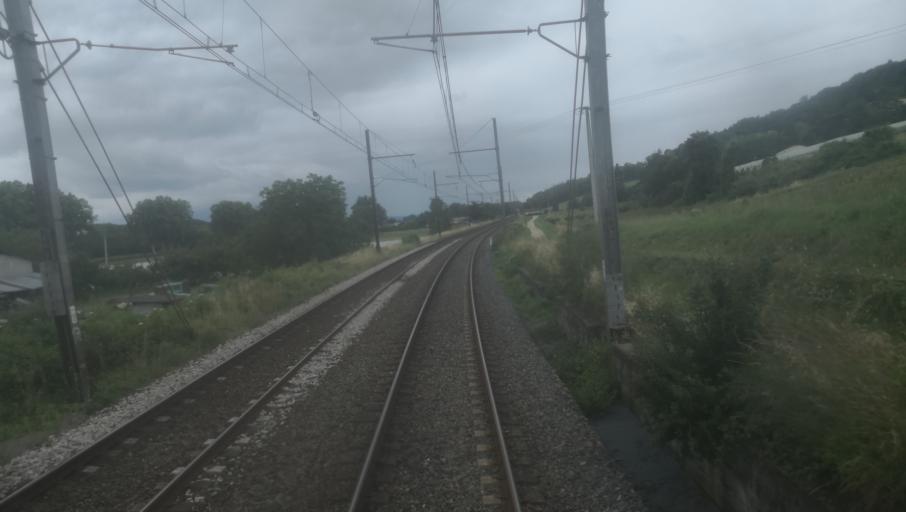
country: FR
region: Aquitaine
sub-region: Departement du Lot-et-Garonne
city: Port-Sainte-Marie
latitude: 44.2388
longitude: 0.4451
